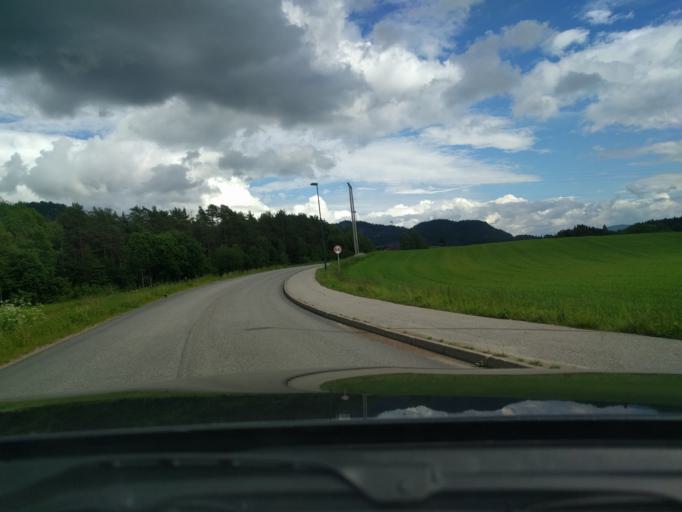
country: NO
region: Telemark
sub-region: Siljan
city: Siljan
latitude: 59.2881
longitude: 9.7145
